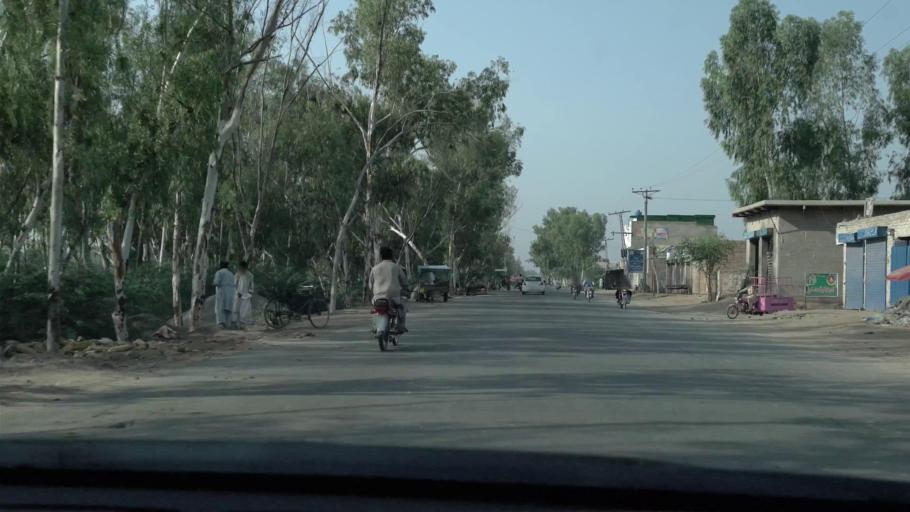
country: PK
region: Punjab
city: Gojra
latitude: 31.1198
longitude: 72.6689
